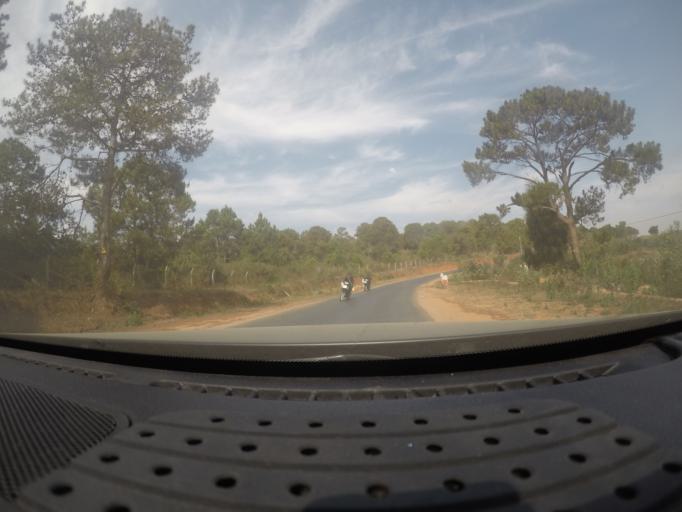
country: MM
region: Shan
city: Taunggyi
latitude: 20.6914
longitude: 96.6284
